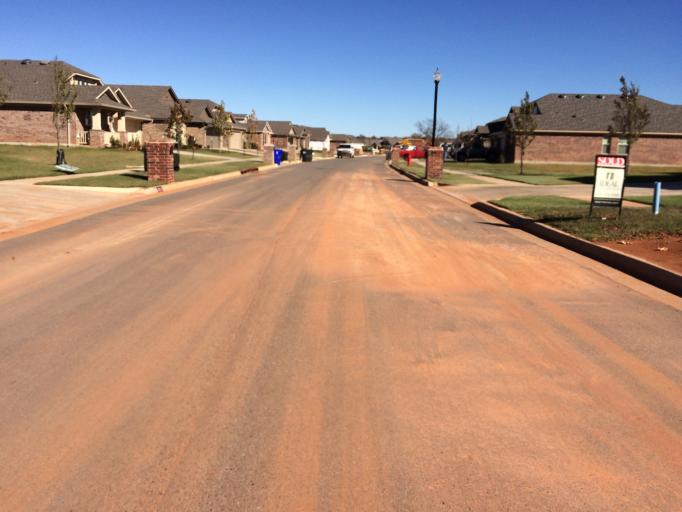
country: US
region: Oklahoma
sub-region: Cleveland County
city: Norman
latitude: 35.2584
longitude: -97.4573
